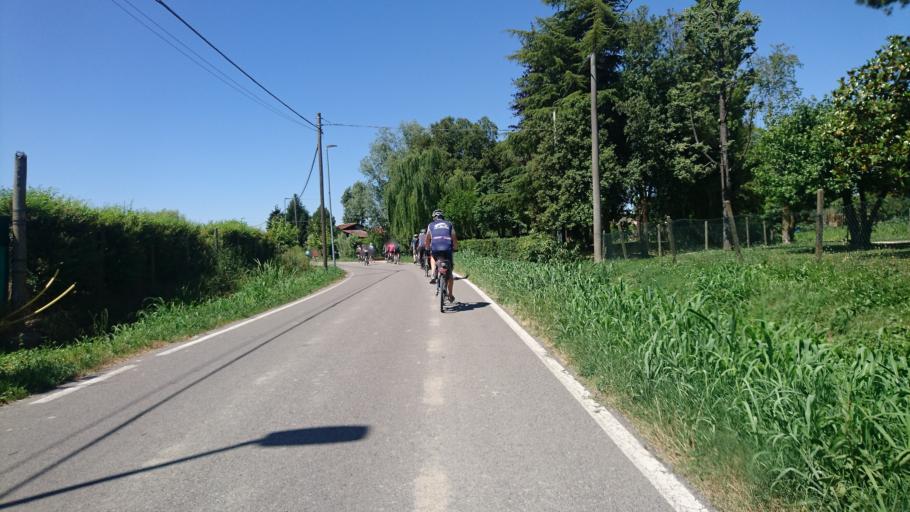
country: IT
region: Veneto
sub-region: Provincia di Padova
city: Bertipaglia
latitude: 45.3048
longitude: 11.8891
